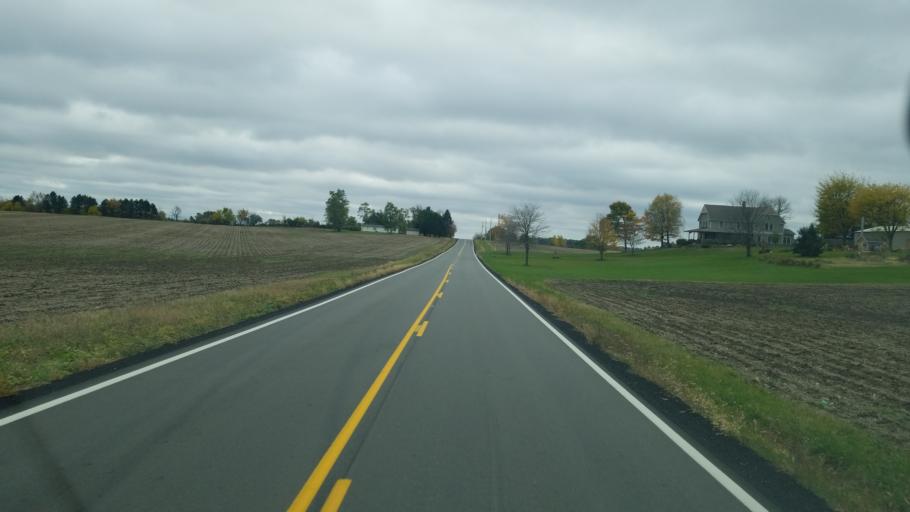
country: US
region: Ohio
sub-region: Huron County
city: Plymouth
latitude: 40.9778
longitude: -82.7109
